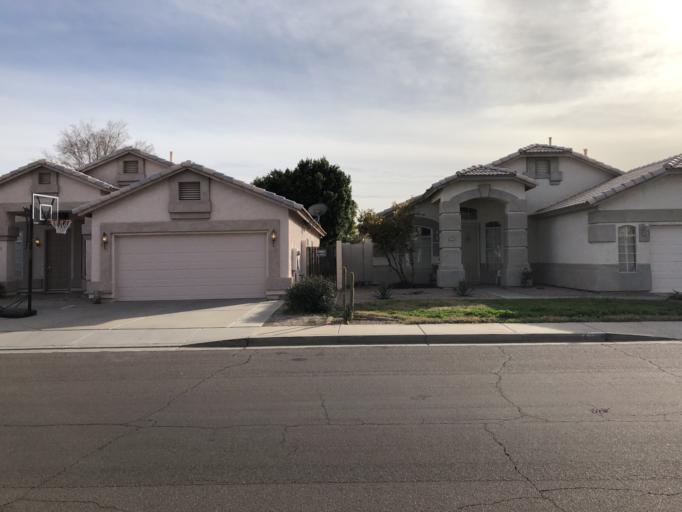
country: US
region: Arizona
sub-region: Maricopa County
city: Guadalupe
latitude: 33.3090
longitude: -111.9253
